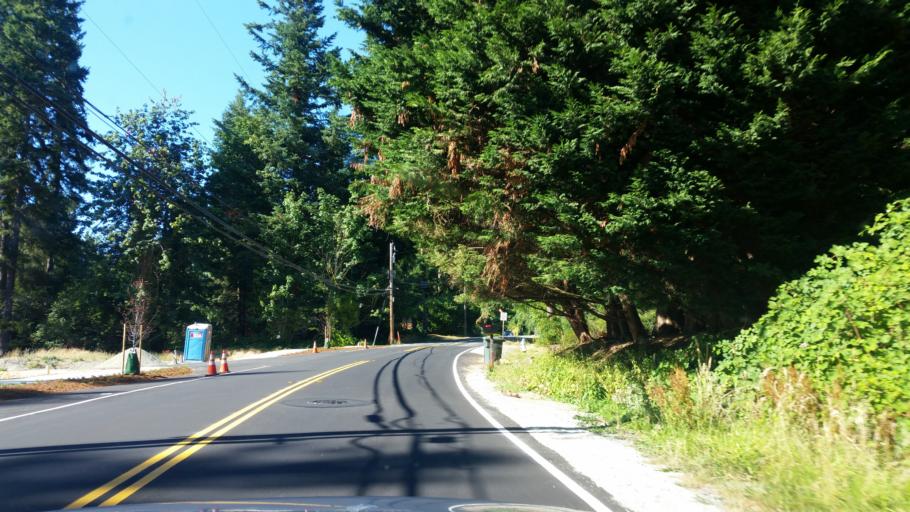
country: US
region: Washington
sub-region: King County
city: Lake Forest Park
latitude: 47.7638
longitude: -122.2855
